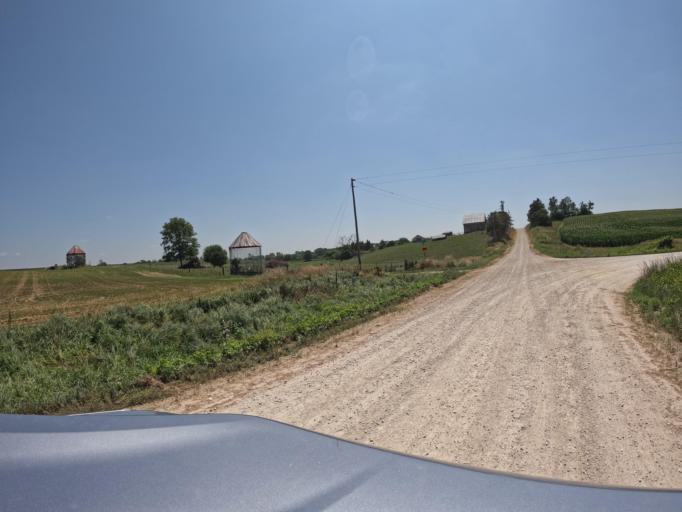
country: US
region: Iowa
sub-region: Keokuk County
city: Sigourney
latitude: 41.2649
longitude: -92.1807
